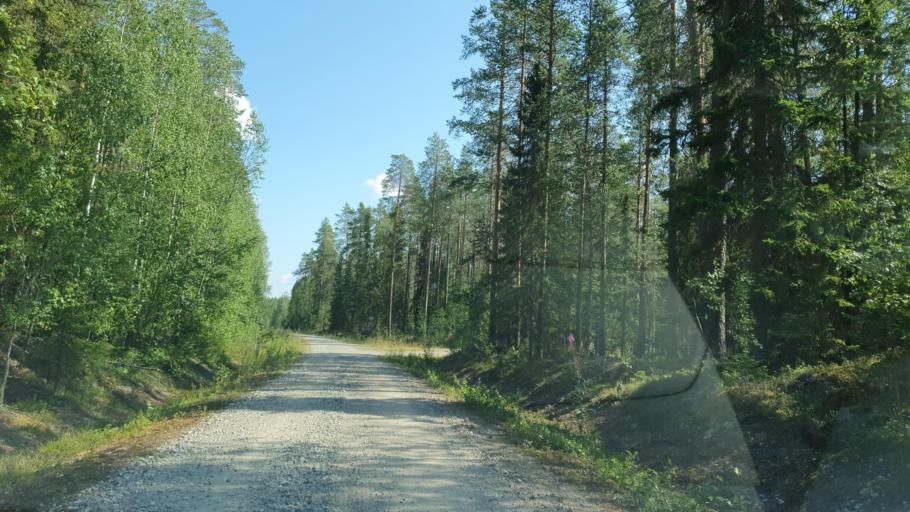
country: FI
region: Kainuu
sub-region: Kehys-Kainuu
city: Kuhmo
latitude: 63.9652
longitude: 29.5431
